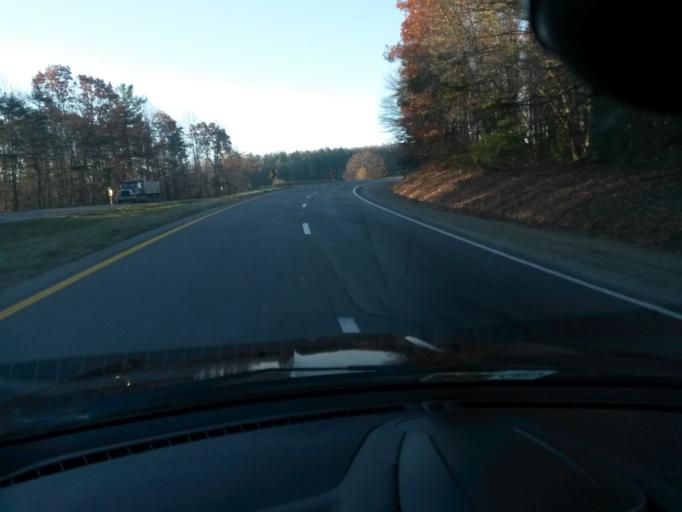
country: US
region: Virginia
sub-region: Franklin County
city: Henry Fork
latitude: 36.8546
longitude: -79.8764
